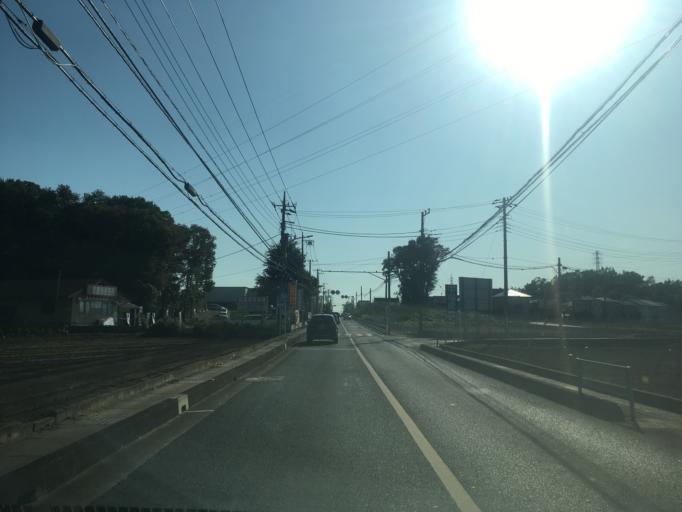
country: JP
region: Saitama
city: Kamifukuoka
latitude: 35.8654
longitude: 139.4715
